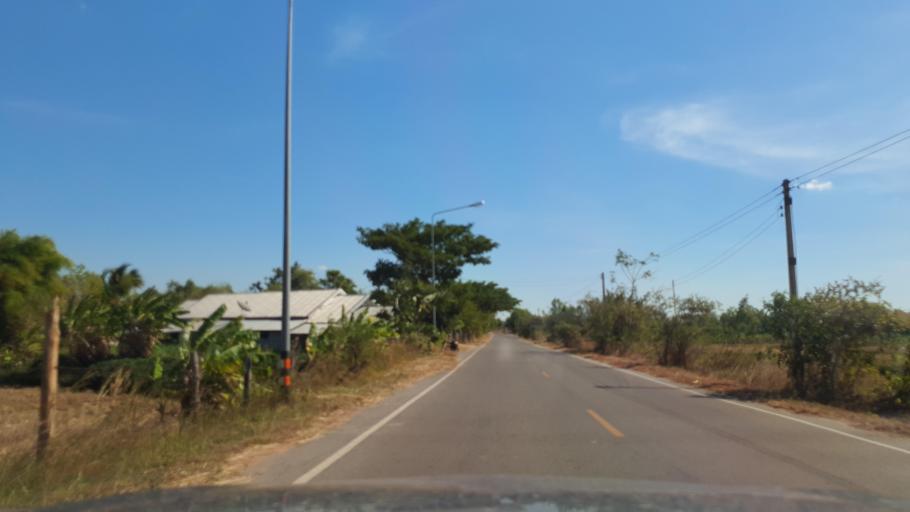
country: TH
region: Kalasin
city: Khao Wong
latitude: 16.7305
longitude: 104.0977
